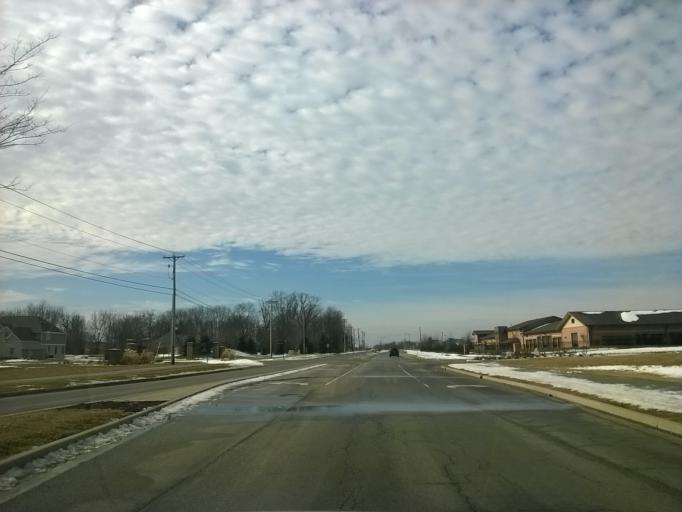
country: US
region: Indiana
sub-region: Boone County
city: Zionsville
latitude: 39.9773
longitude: -86.2168
